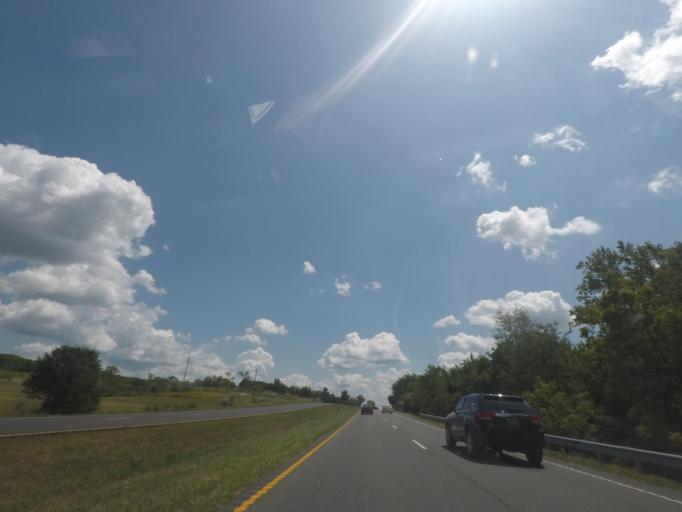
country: US
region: Virginia
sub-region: City of Winchester
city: Winchester
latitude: 39.0949
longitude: -78.1038
